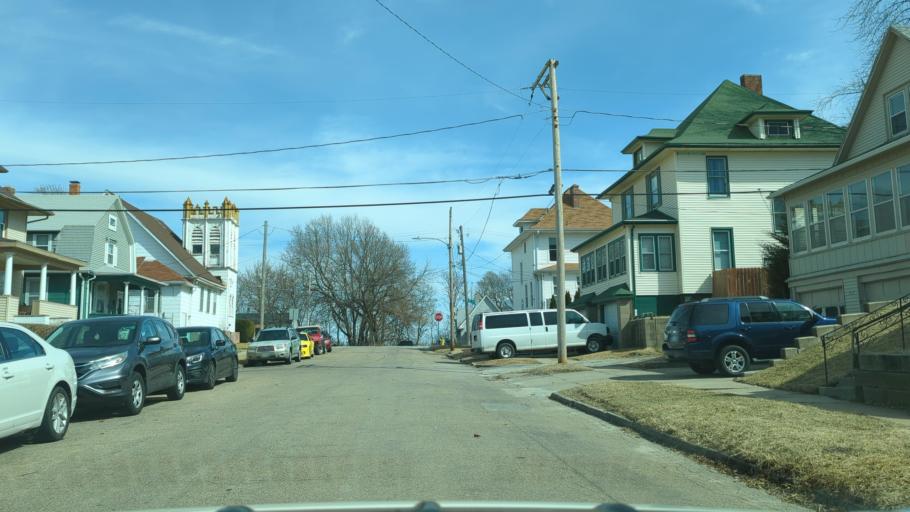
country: US
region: Nebraska
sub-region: Douglas County
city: Omaha
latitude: 41.2360
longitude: -95.9305
